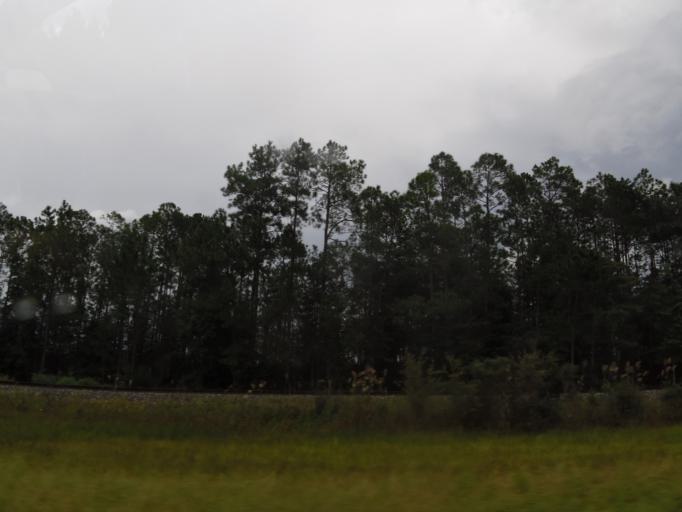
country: US
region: Georgia
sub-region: Wayne County
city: Jesup
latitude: 31.4917
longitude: -81.7449
